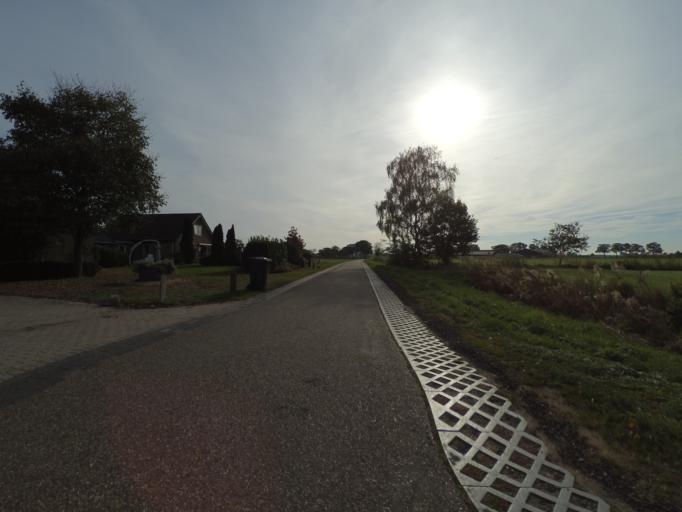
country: NL
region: Overijssel
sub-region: Gemeente Raalte
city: Raalte
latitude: 52.3619
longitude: 6.3655
